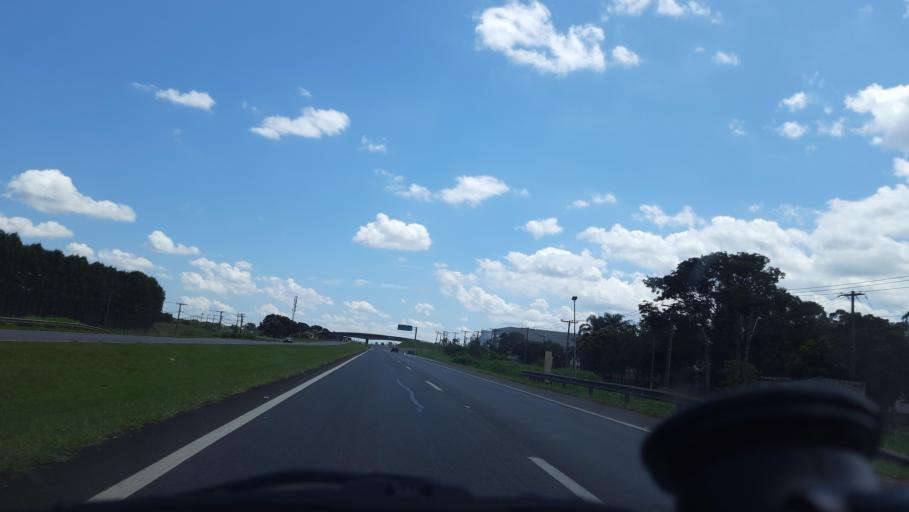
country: BR
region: Sao Paulo
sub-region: Moji-Guacu
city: Mogi-Gaucu
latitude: -22.3259
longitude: -46.9615
